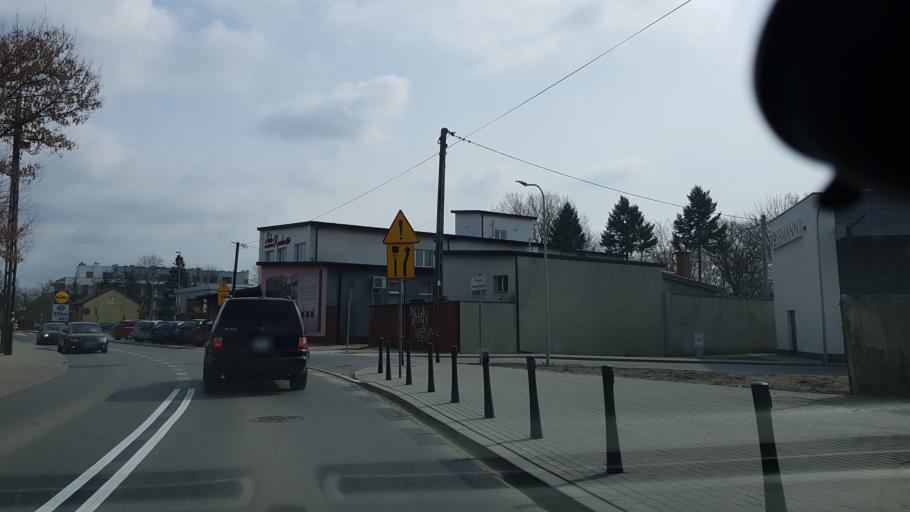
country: PL
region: Masovian Voivodeship
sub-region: Warszawa
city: Rembertow
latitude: 52.2592
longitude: 21.1560
